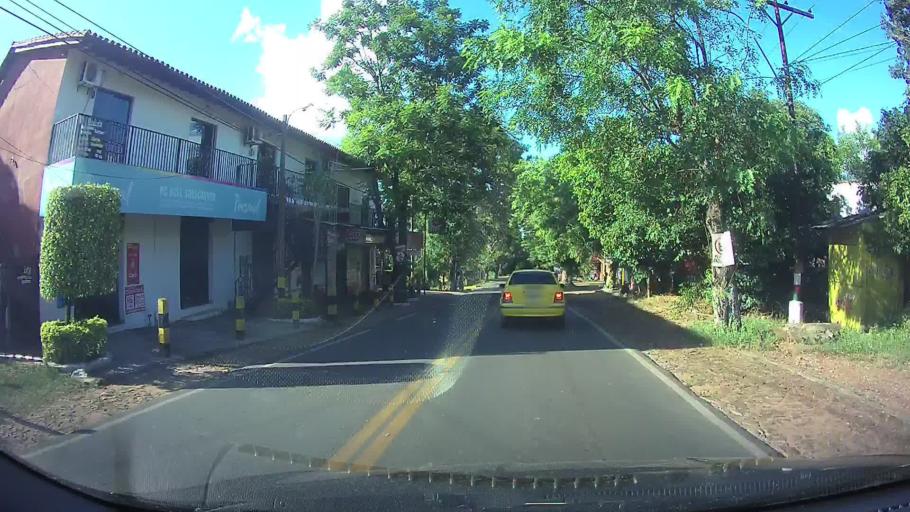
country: PY
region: Central
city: Aregua
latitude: -25.3187
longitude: -57.3883
